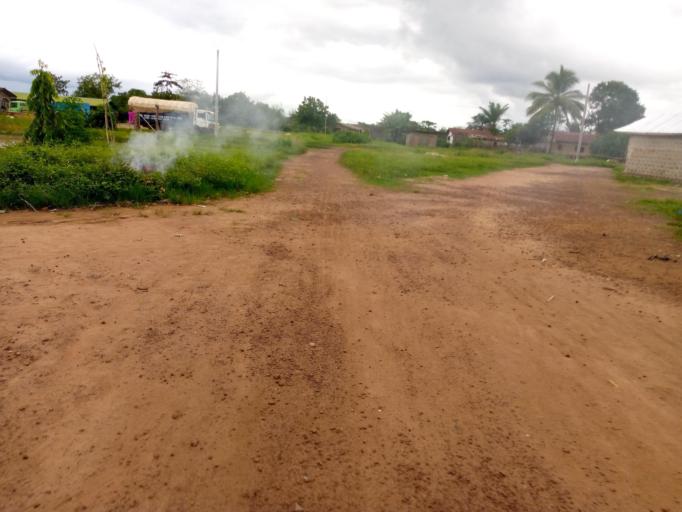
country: SL
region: Southern Province
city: Moyamba
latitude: 8.1530
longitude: -12.4370
